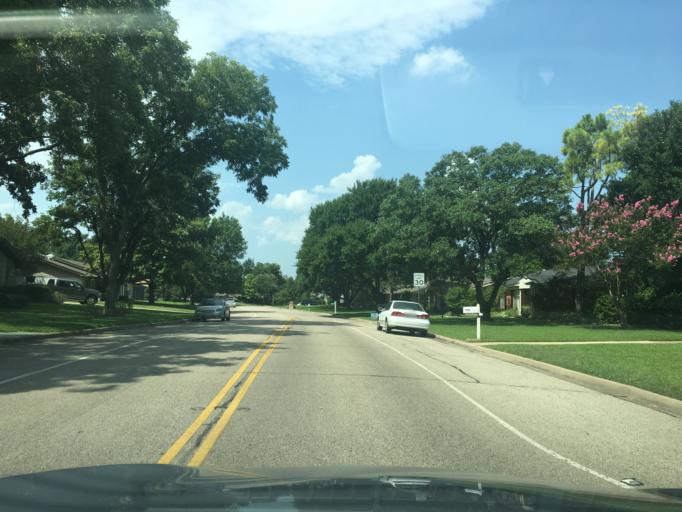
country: US
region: Texas
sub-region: Dallas County
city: Farmers Branch
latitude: 32.9338
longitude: -96.8672
